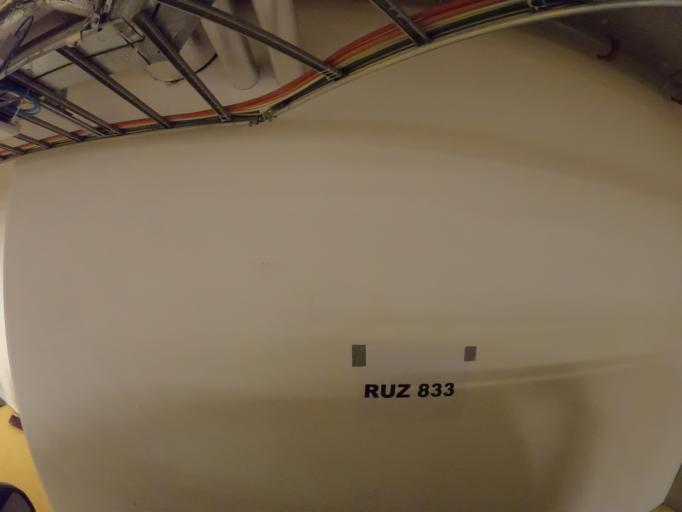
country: SE
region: Skane
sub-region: Osby Kommun
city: Lonsboda
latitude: 56.4070
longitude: 14.2166
